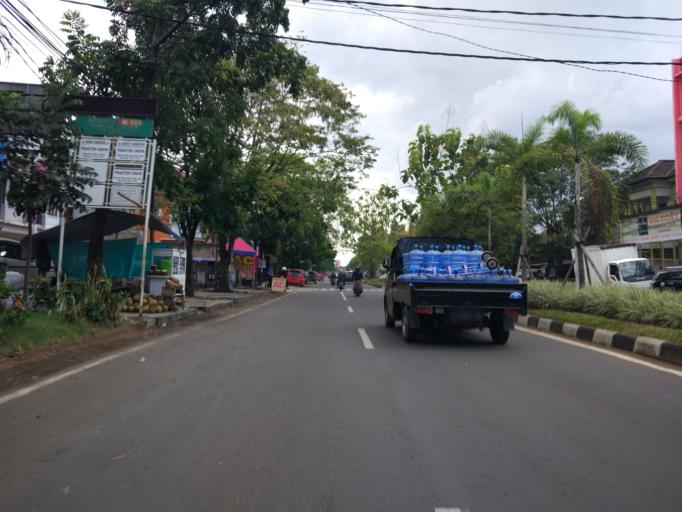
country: ID
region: West Java
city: Bandung
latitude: -6.9145
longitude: 107.6636
